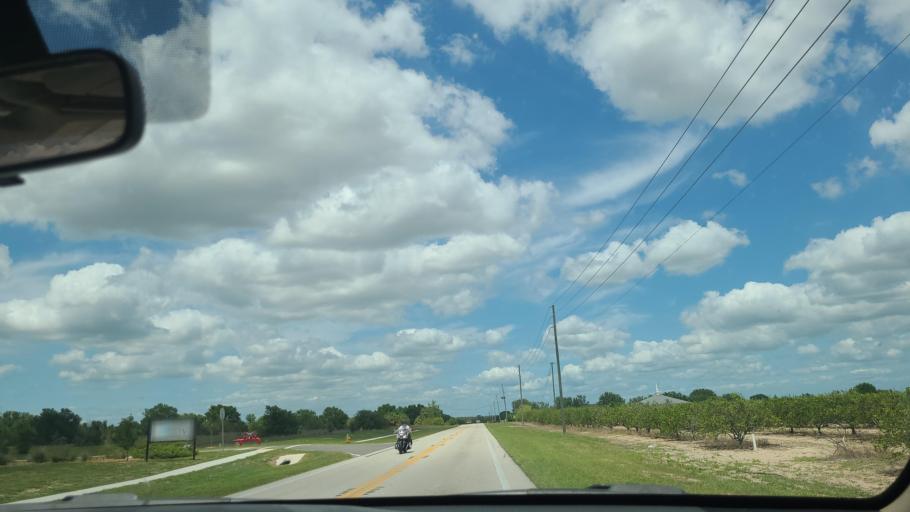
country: US
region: Florida
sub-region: Polk County
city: Lake Wales
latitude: 27.9030
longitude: -81.5560
